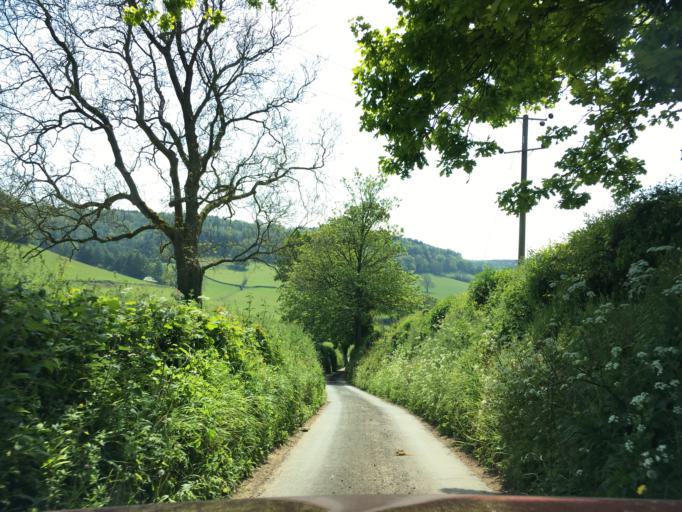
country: GB
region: England
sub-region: Gloucestershire
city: Dursley
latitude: 51.6660
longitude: -2.3375
